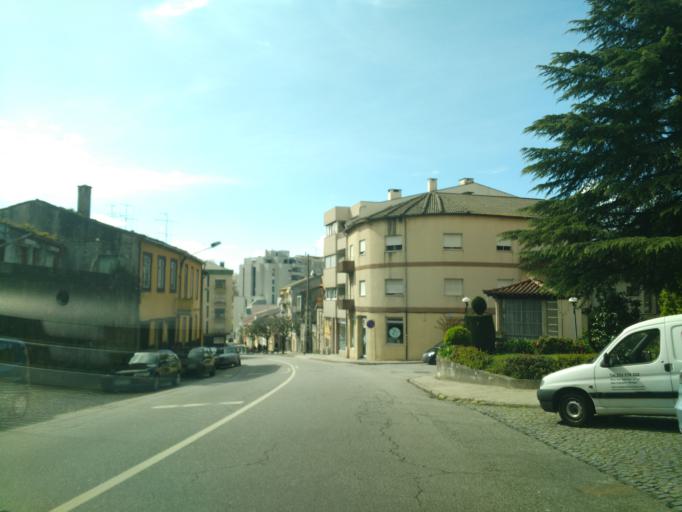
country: PT
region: Braga
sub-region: Braga
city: Braga
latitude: 41.5423
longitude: -8.4150
